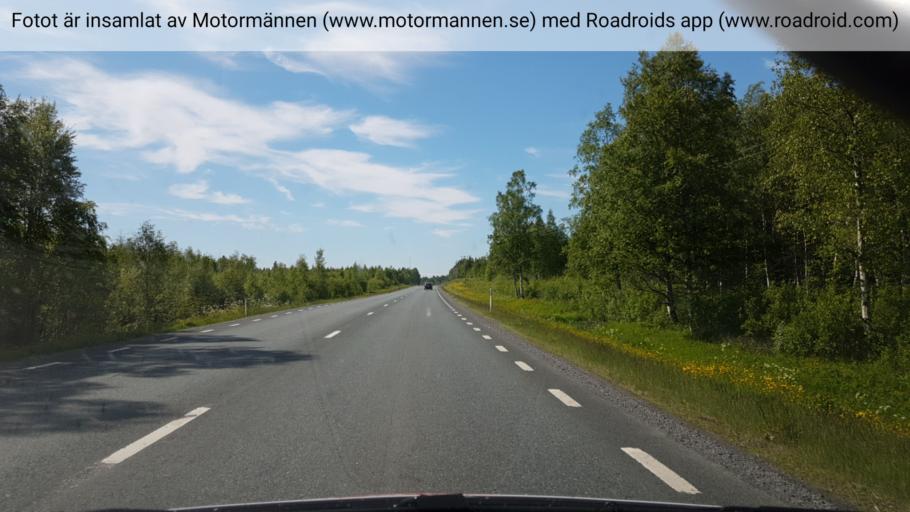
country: SE
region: Norrbotten
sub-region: Haparanda Kommun
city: Haparanda
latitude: 65.8226
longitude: 24.0578
